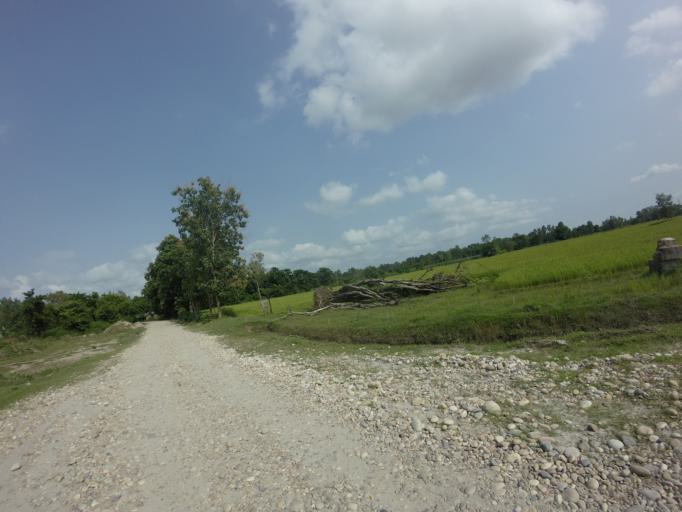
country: NP
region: Far Western
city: Tikapur
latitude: 28.4445
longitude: 81.0737
